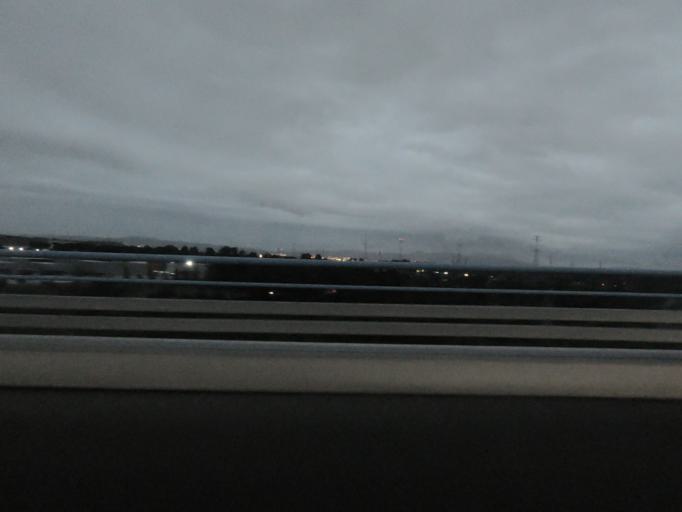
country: PT
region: Setubal
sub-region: Seixal
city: Aldeia de Paio Pires
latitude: 38.5921
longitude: -9.0565
